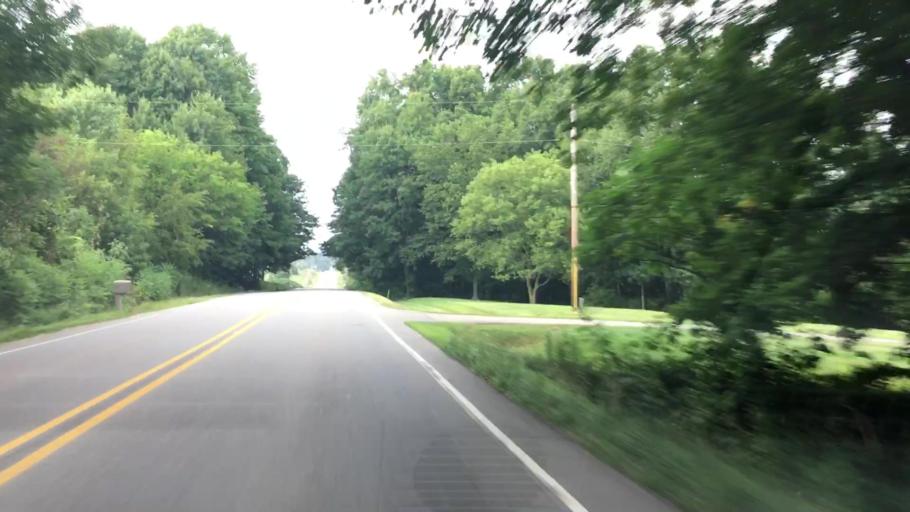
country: US
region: Michigan
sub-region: Ottawa County
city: Hudsonville
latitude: 42.8411
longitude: -85.9006
